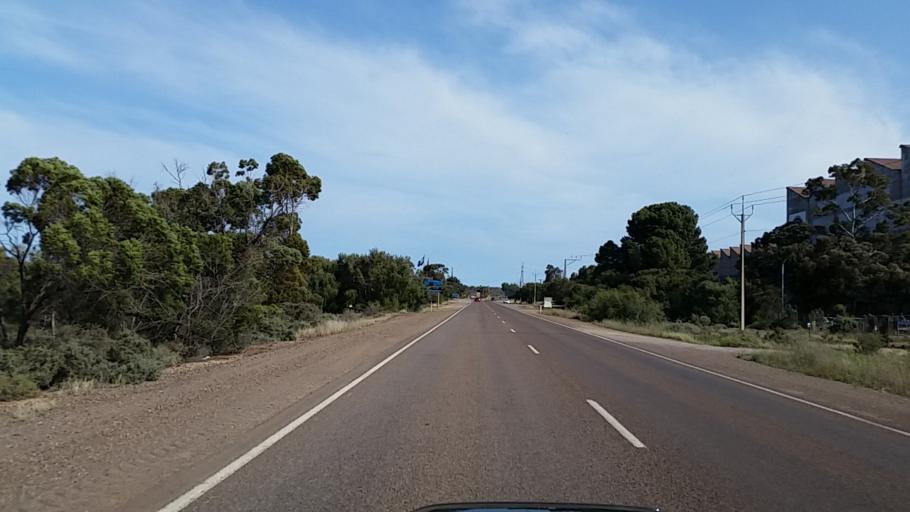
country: AU
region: South Australia
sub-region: Whyalla
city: Whyalla
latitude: -33.0039
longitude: 137.5764
